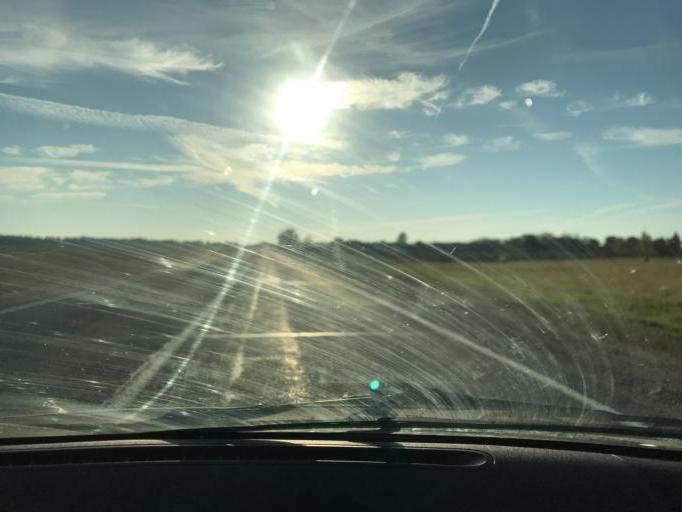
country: BY
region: Brest
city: Horad Kobryn
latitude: 52.2142
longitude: 24.4881
